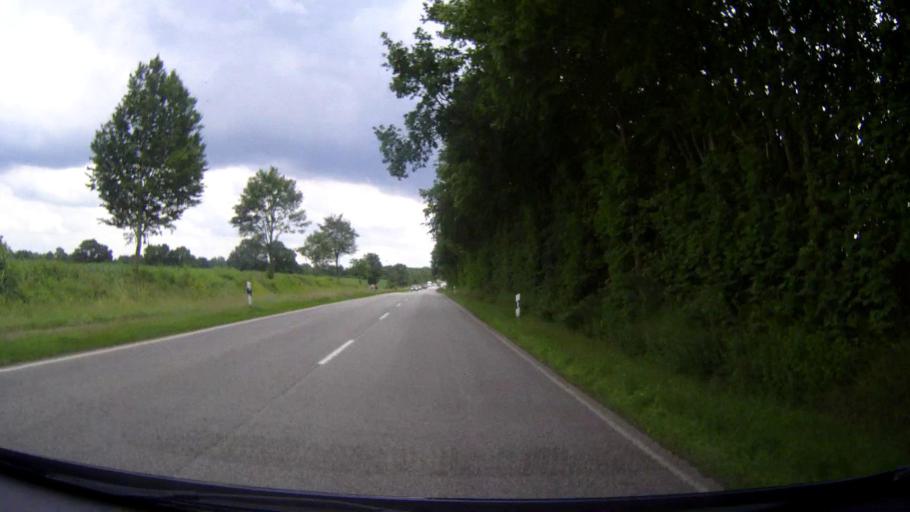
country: DE
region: Schleswig-Holstein
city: Schenefeld
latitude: 54.0631
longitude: 9.4745
